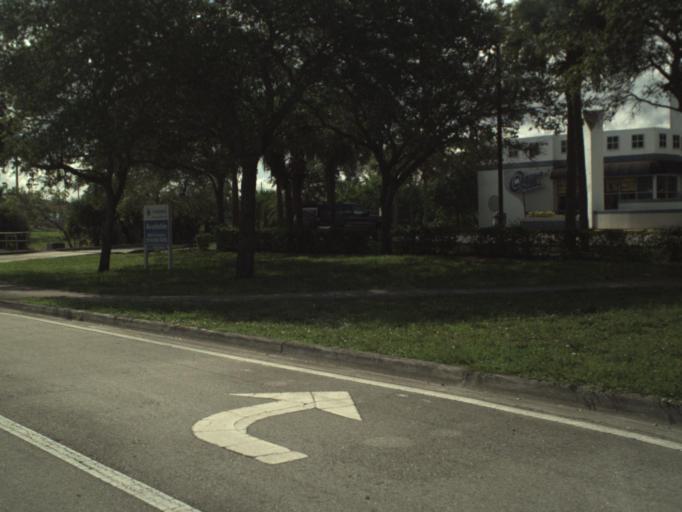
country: US
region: Florida
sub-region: Broward County
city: Plantation
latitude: 26.1665
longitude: -80.2522
